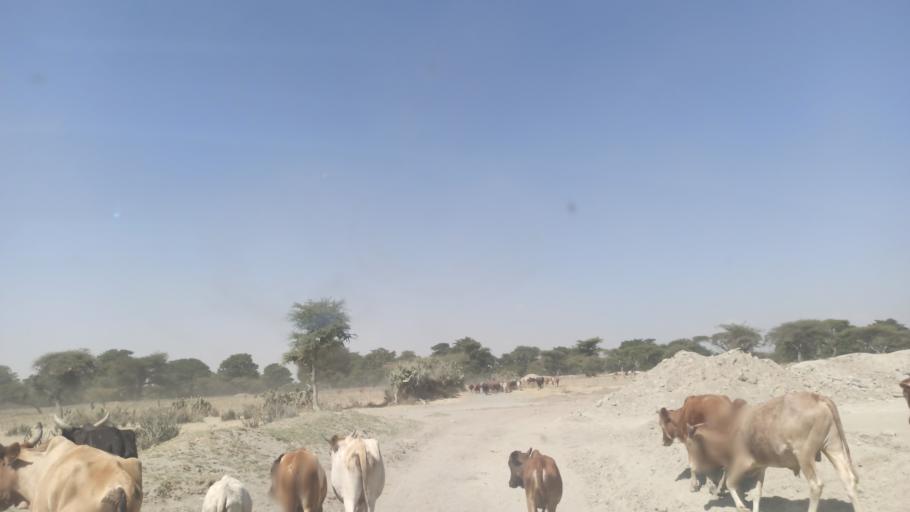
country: ET
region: Oromiya
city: Ziway
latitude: 7.7015
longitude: 38.6408
